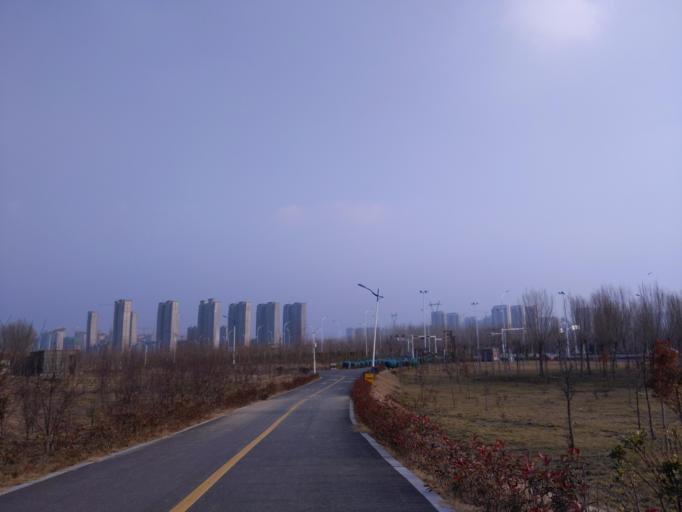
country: CN
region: Henan Sheng
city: Puyang
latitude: 35.8198
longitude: 114.9991
